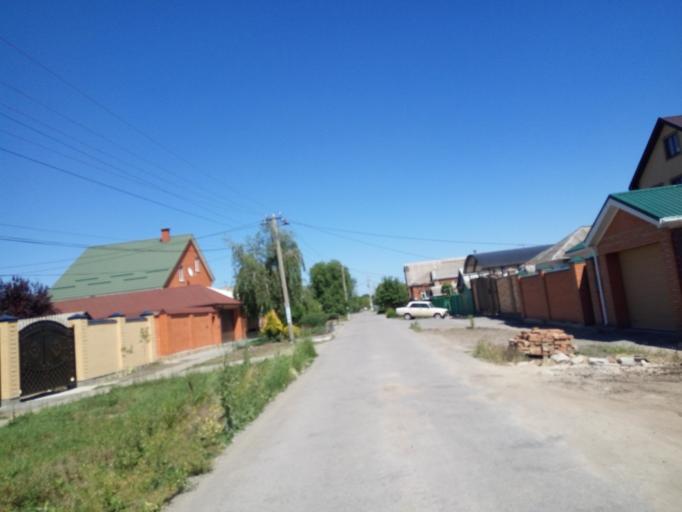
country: RU
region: Rostov
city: Bataysk
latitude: 47.1235
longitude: 39.7358
